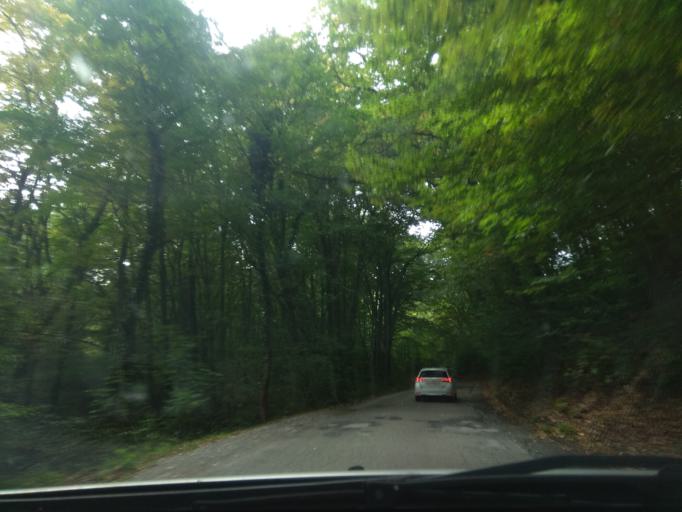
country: HU
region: Borsod-Abauj-Zemplen
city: Miskolc
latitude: 48.0659
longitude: 20.6828
